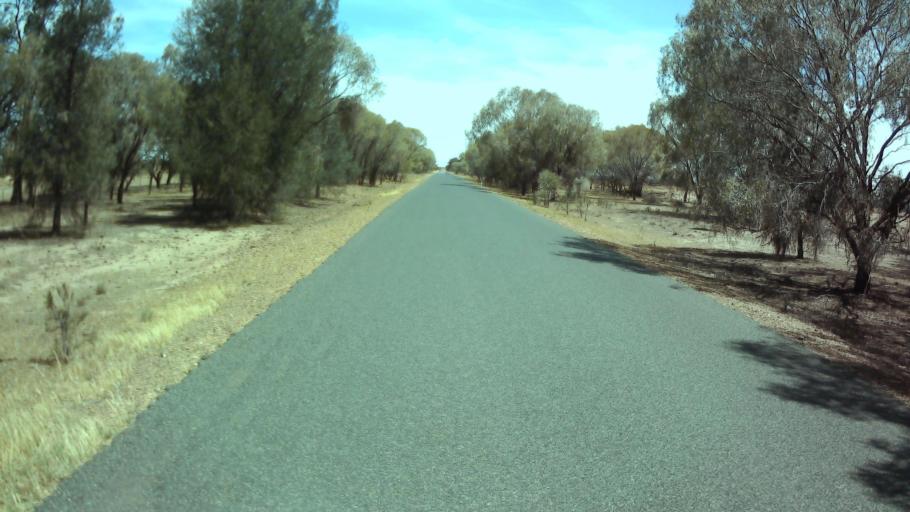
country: AU
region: New South Wales
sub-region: Weddin
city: Grenfell
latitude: -33.8743
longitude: 147.7441
